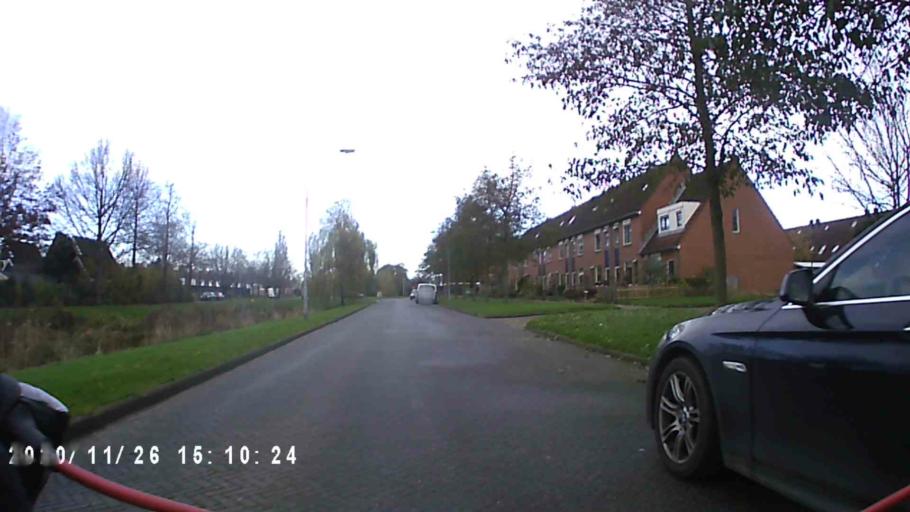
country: NL
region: Groningen
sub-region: Gemeente Appingedam
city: Appingedam
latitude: 53.3178
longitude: 6.8470
